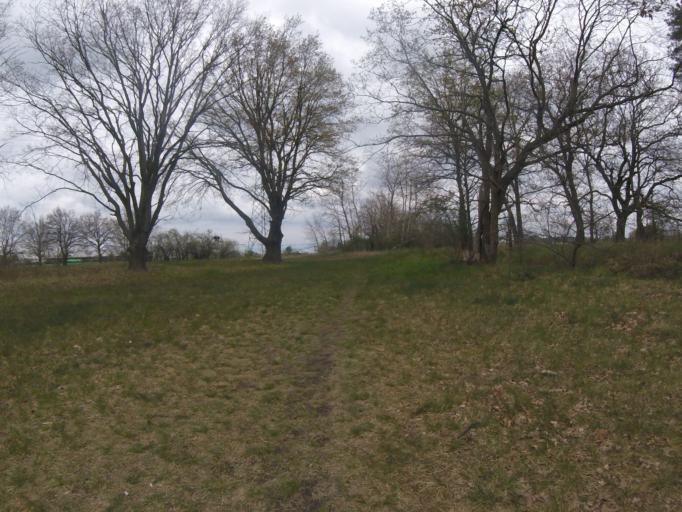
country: DE
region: Brandenburg
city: Mittenwalde
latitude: 52.2542
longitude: 13.5656
